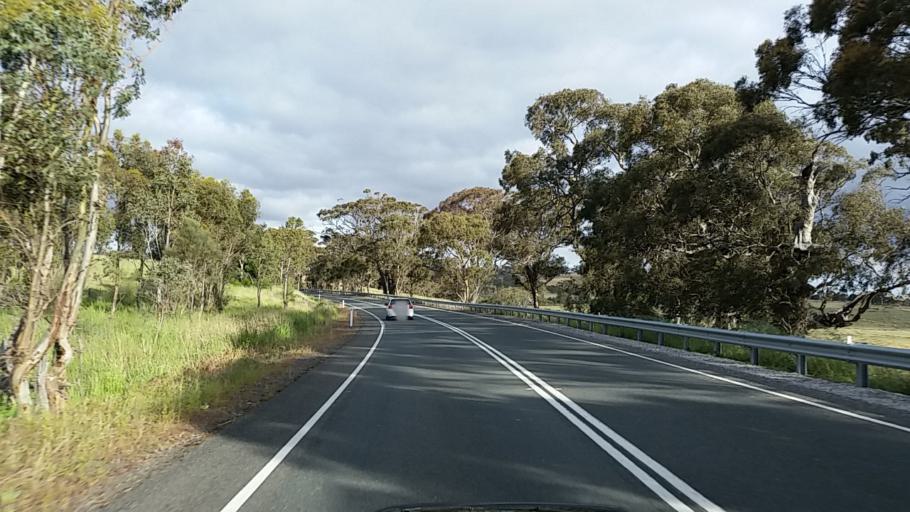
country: AU
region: South Australia
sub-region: Barossa
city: Angaston
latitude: -34.5728
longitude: 139.1577
